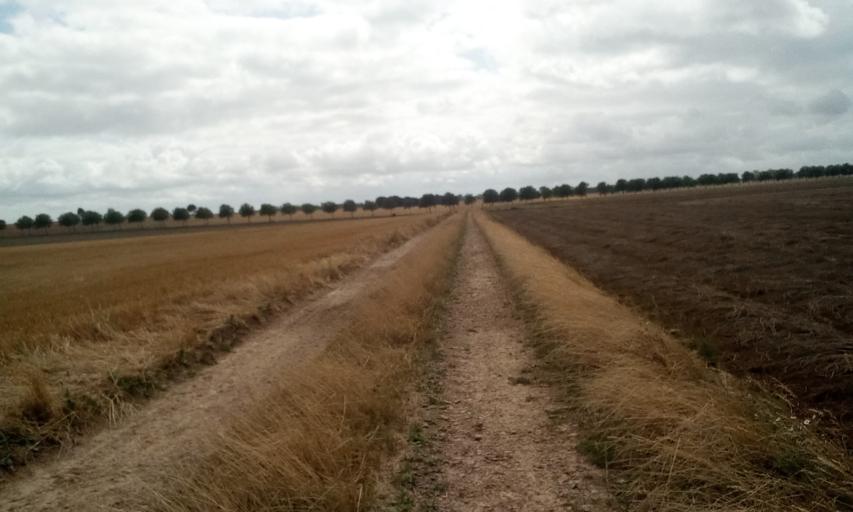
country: FR
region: Lower Normandy
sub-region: Departement du Calvados
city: Cheux
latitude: 49.1788
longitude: -0.5430
